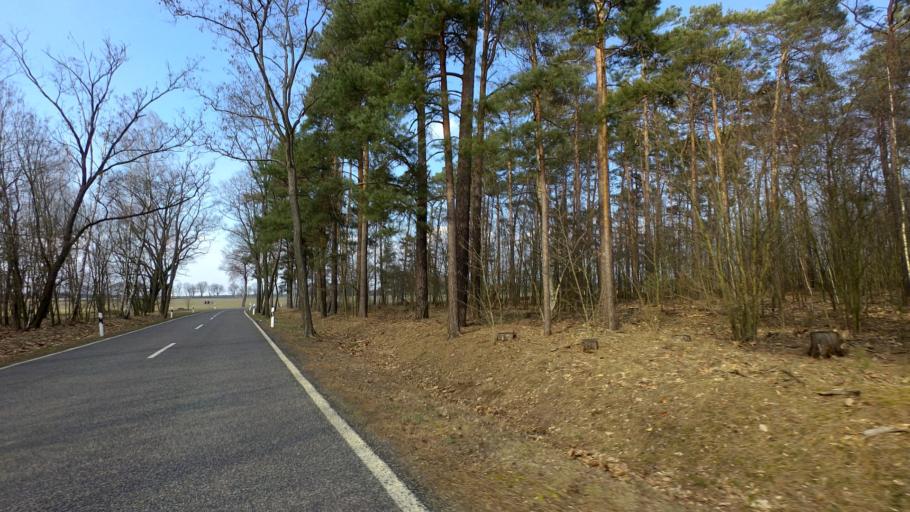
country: DE
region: Brandenburg
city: Dahme
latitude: 51.9591
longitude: 13.4352
